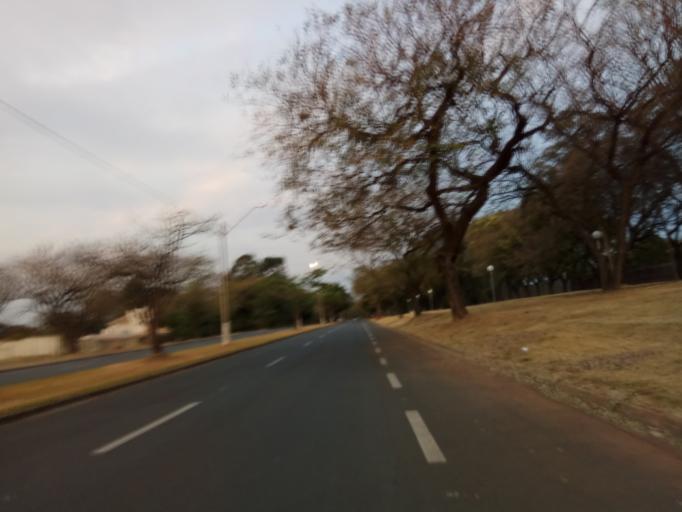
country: BR
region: Sao Paulo
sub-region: Piracicaba
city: Piracicaba
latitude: -22.7527
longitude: -47.5931
